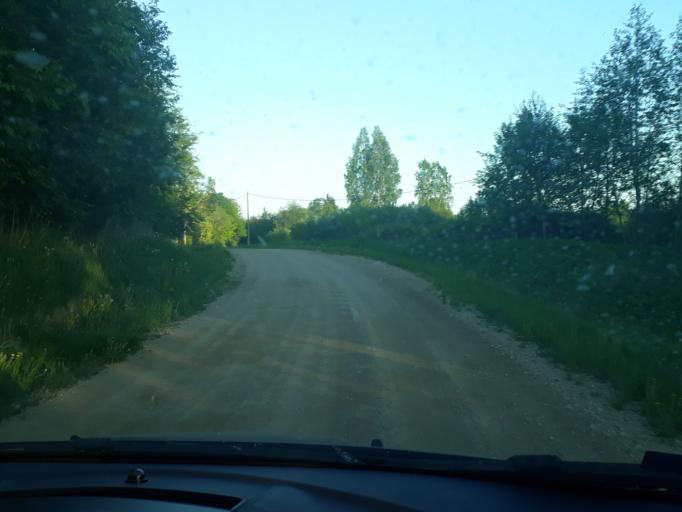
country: EE
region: Paernumaa
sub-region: Vaendra vald (alev)
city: Vandra
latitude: 58.5677
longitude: 24.9465
